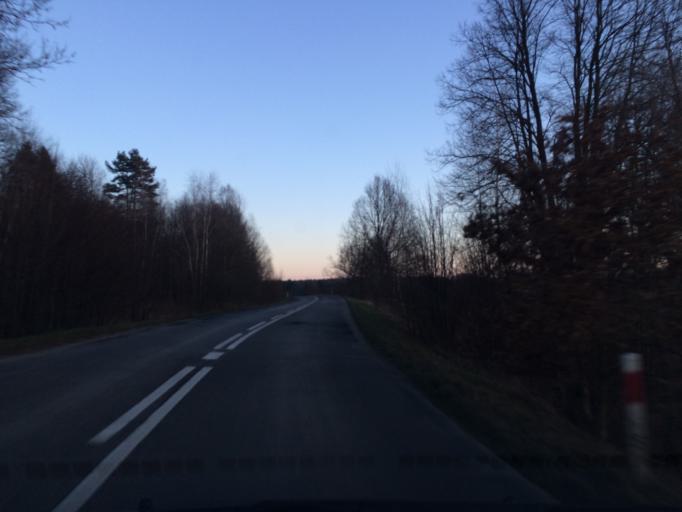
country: PL
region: Lower Silesian Voivodeship
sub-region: Powiat lwowecki
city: Lwowek Slaski
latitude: 51.1188
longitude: 15.6416
